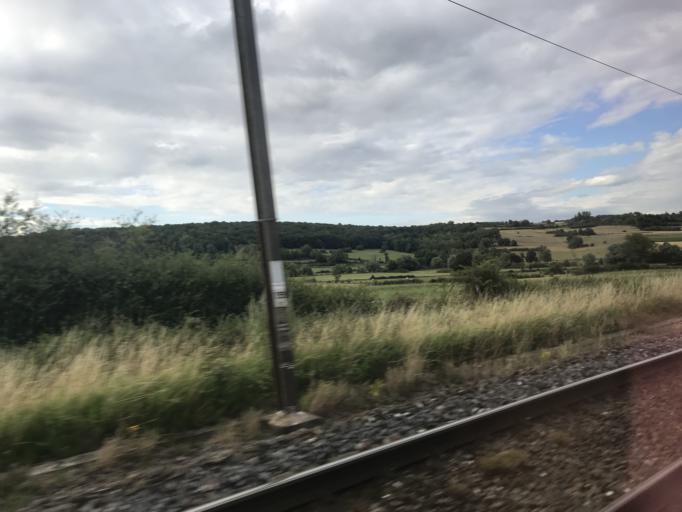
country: FR
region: Lorraine
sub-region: Departement de la Meuse
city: Montmedy
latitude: 49.5282
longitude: 5.2796
